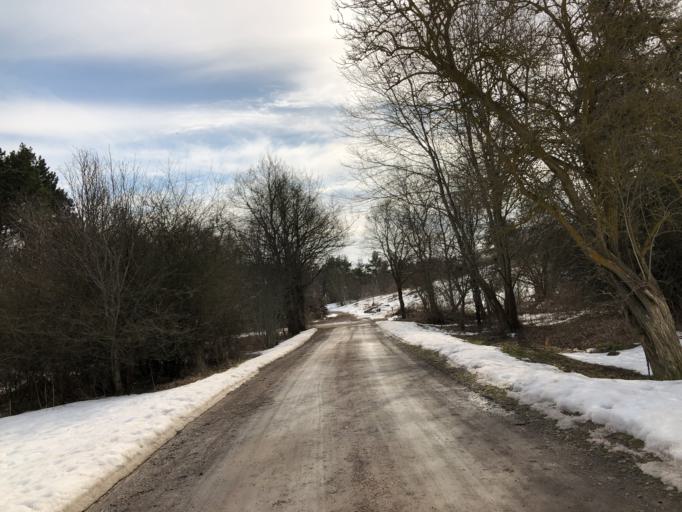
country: SE
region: Kalmar
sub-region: Kalmar Kommun
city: Kalmar
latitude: 56.6596
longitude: 16.3177
